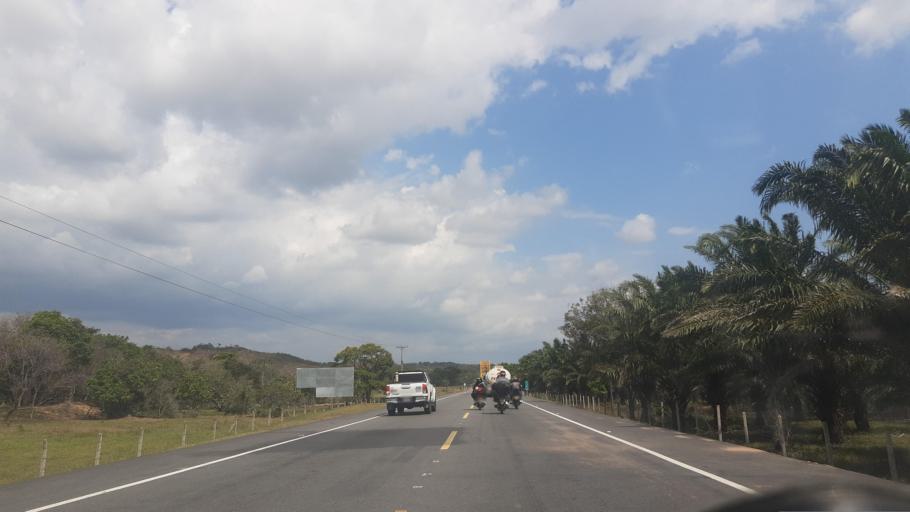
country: CO
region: Casanare
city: Tauramena
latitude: 4.9205
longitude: -72.6744
